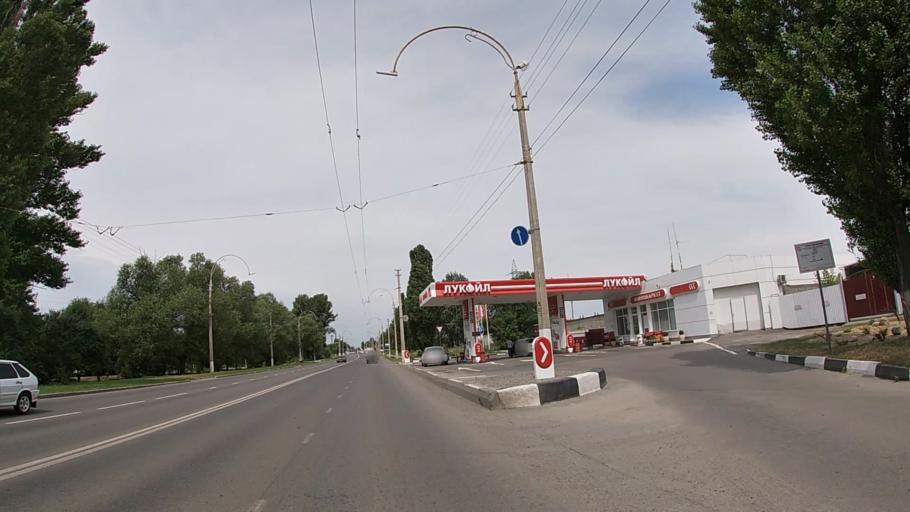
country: RU
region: Belgorod
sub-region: Belgorodskiy Rayon
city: Belgorod
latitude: 50.6105
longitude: 36.5429
